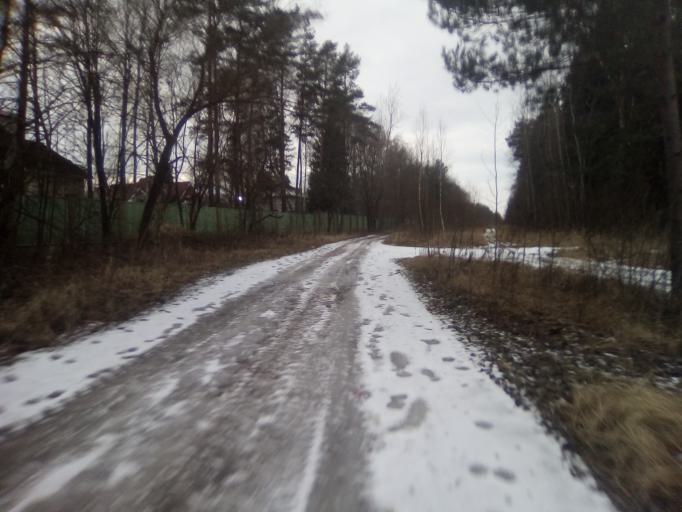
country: RU
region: Moskovskaya
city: Filimonki
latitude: 55.5126
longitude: 37.3996
